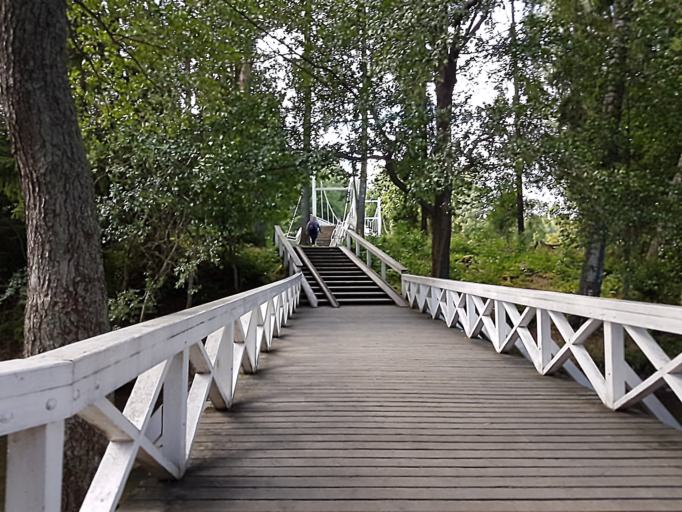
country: FI
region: Pirkanmaa
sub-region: Etelae-Pirkanmaa
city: Valkeakoski
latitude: 61.2722
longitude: 24.0485
